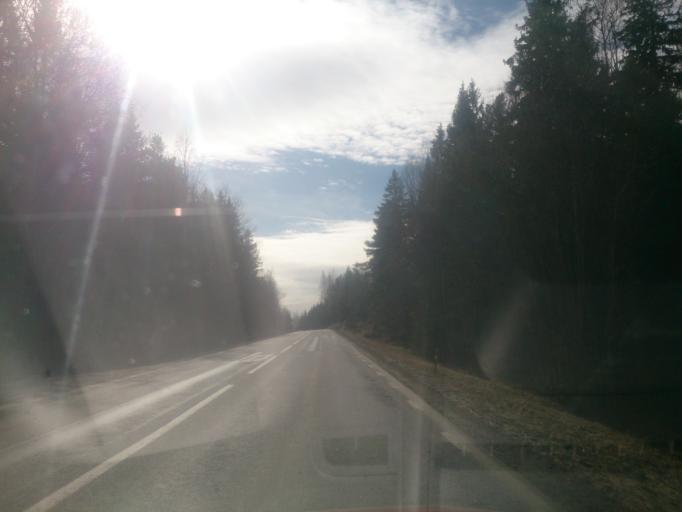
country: SE
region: OEstergoetland
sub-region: Finspangs Kommun
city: Finspang
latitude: 58.6150
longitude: 15.8110
